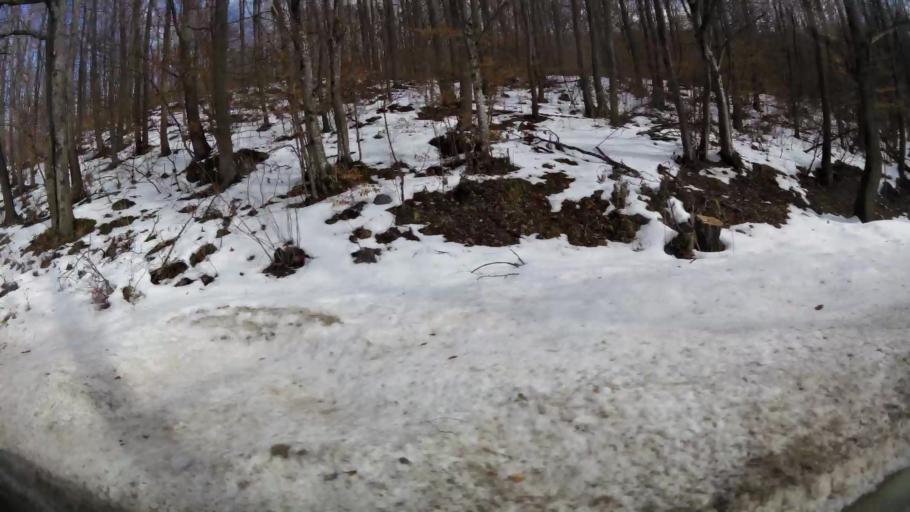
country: BG
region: Sofia-Capital
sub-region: Stolichna Obshtina
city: Sofia
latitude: 42.6330
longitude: 23.2249
